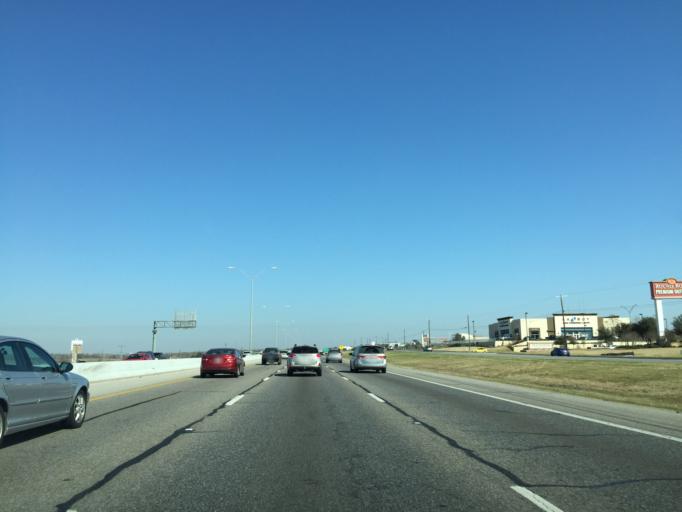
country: US
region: Texas
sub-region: Williamson County
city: Round Rock
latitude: 30.5671
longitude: -97.6926
